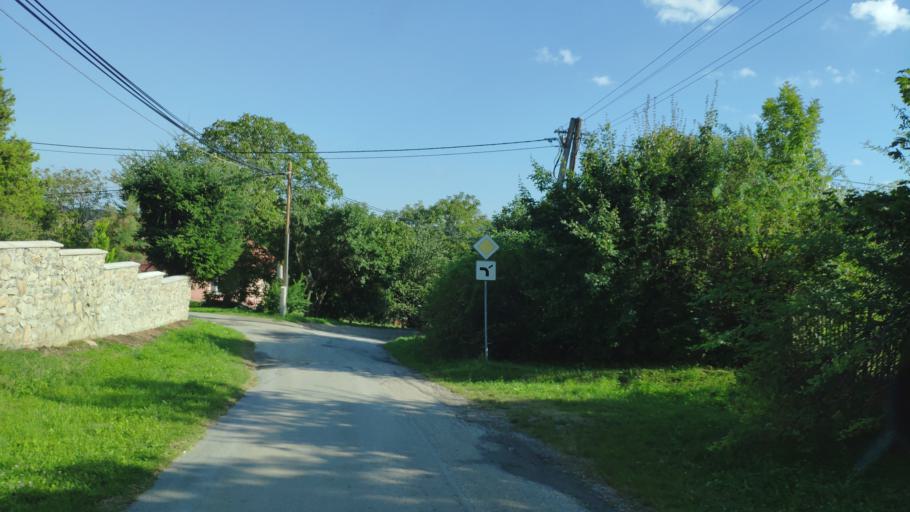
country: SK
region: Kosicky
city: Secovce
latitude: 48.6321
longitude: 21.4773
